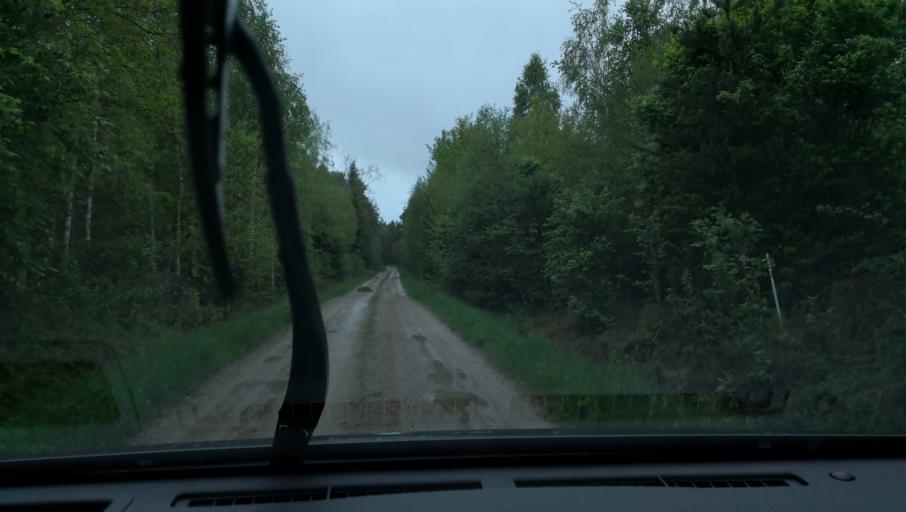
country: SE
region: Uppsala
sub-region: Enkopings Kommun
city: Orsundsbro
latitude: 59.9245
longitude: 17.3396
